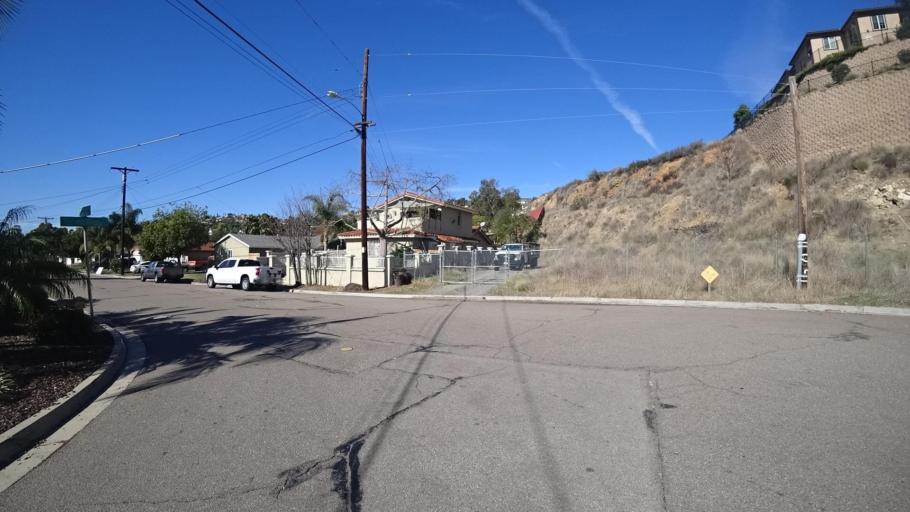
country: US
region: California
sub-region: San Diego County
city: La Presa
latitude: 32.7205
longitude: -116.9747
